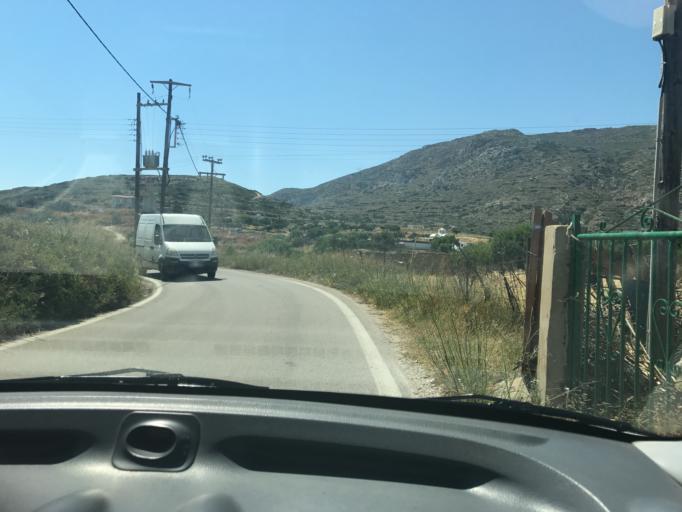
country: GR
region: South Aegean
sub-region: Nomos Dodekanisou
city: Karpathos
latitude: 35.4896
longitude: 27.1577
